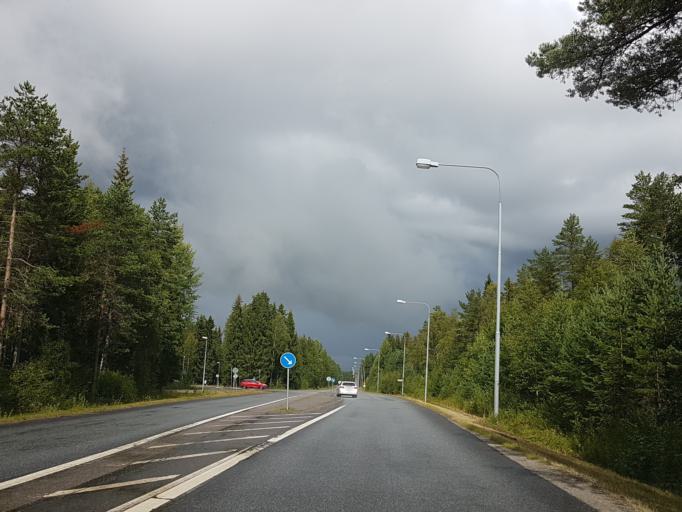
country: SE
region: Vaesterbotten
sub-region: Umea Kommun
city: Ersmark
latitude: 63.8516
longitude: 20.3437
